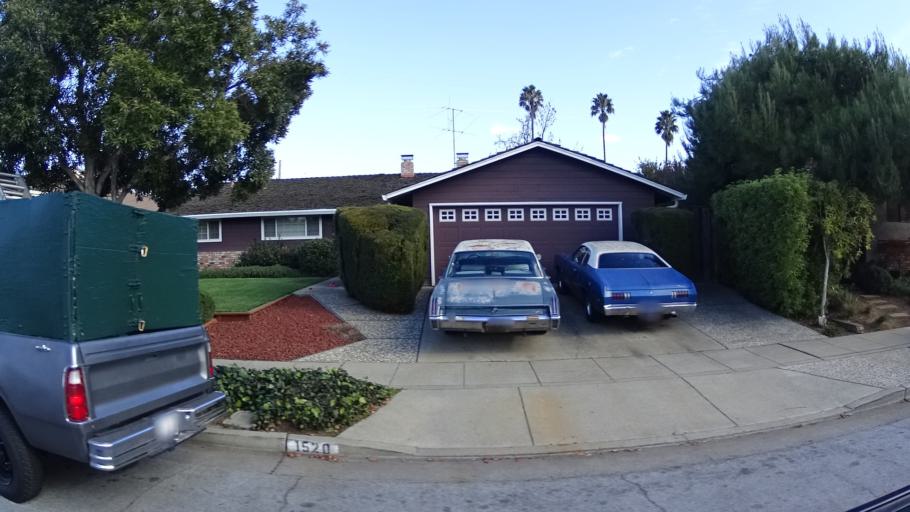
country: US
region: California
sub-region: Santa Clara County
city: Cupertino
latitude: 37.3440
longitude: -122.0490
